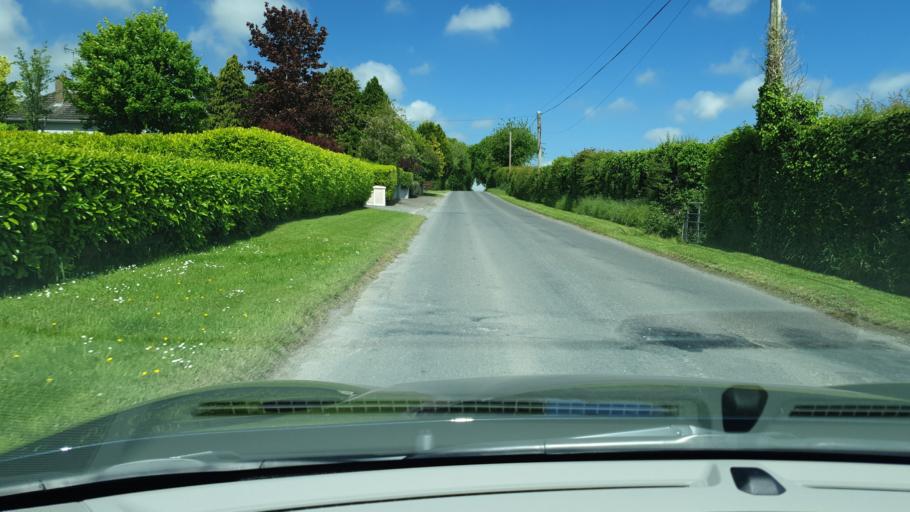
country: IE
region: Leinster
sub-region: Lu
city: Ardee
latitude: 53.8440
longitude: -6.6556
